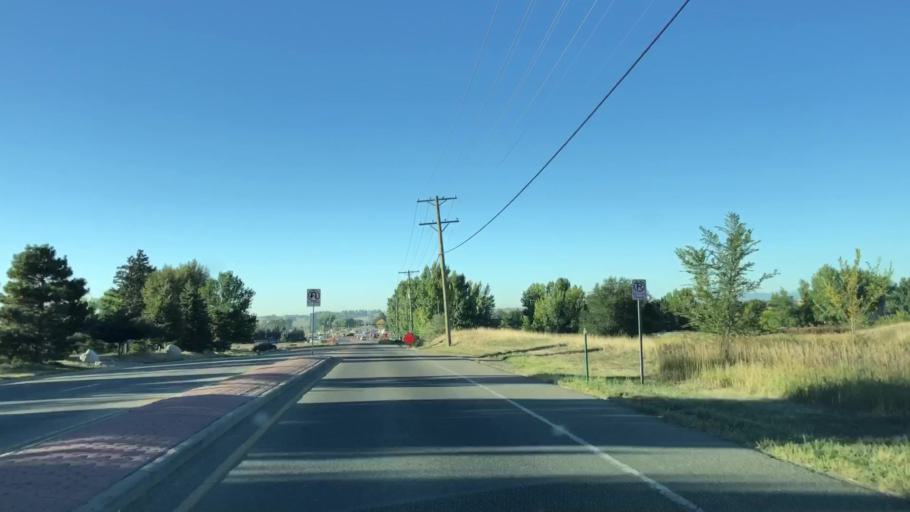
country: US
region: Colorado
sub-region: Larimer County
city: Loveland
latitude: 40.4115
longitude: -105.0211
